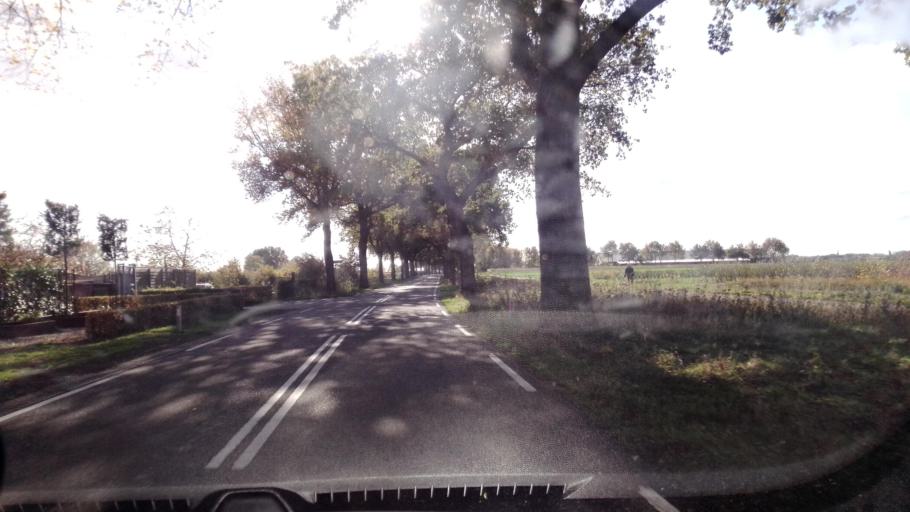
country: NL
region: Limburg
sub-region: Gemeente Venlo
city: Arcen
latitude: 51.4340
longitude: 6.1488
